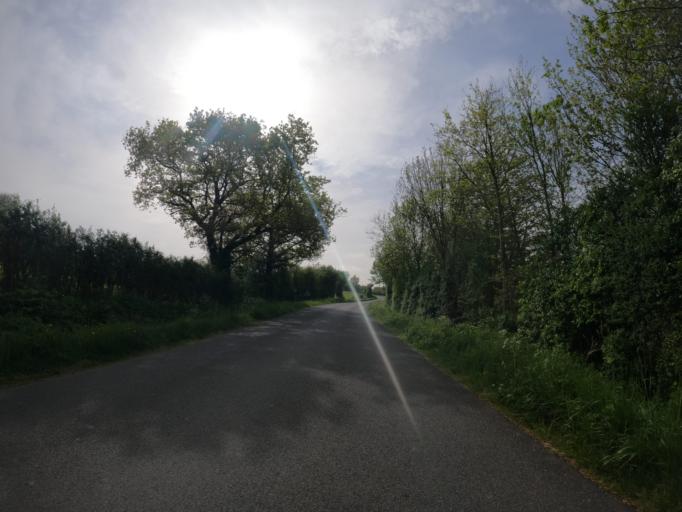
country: FR
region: Poitou-Charentes
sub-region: Departement des Deux-Sevres
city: Moncoutant
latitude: 46.7000
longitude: -0.5258
